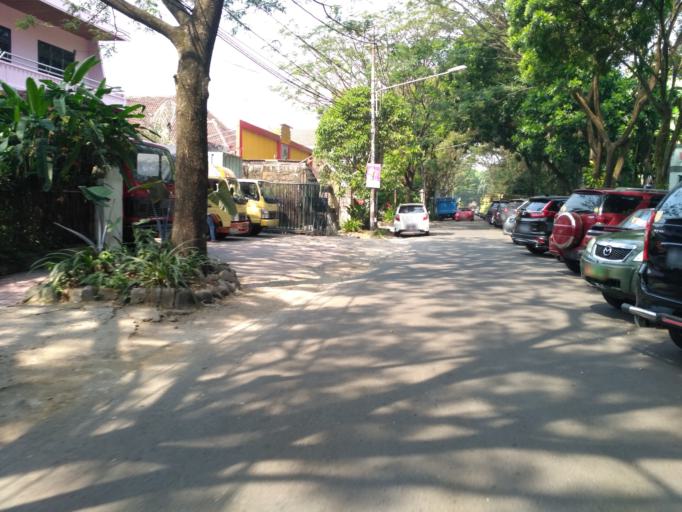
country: ID
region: East Java
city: Malang
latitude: -7.9758
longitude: 112.6356
